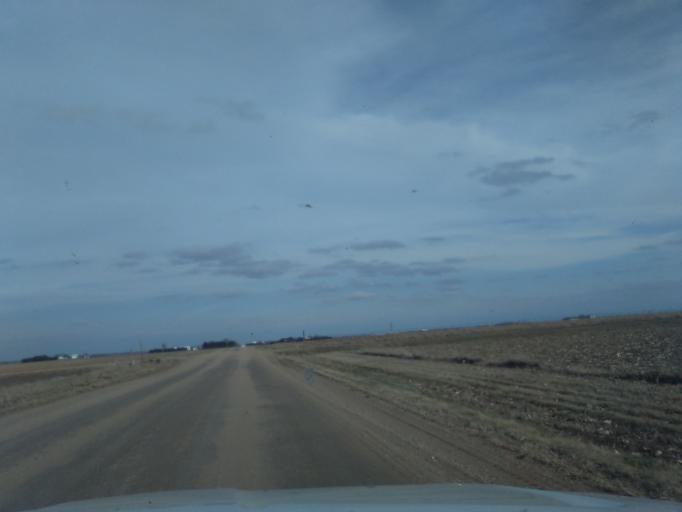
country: US
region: Nebraska
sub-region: Gage County
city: Beatrice
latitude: 40.3209
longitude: -96.8998
